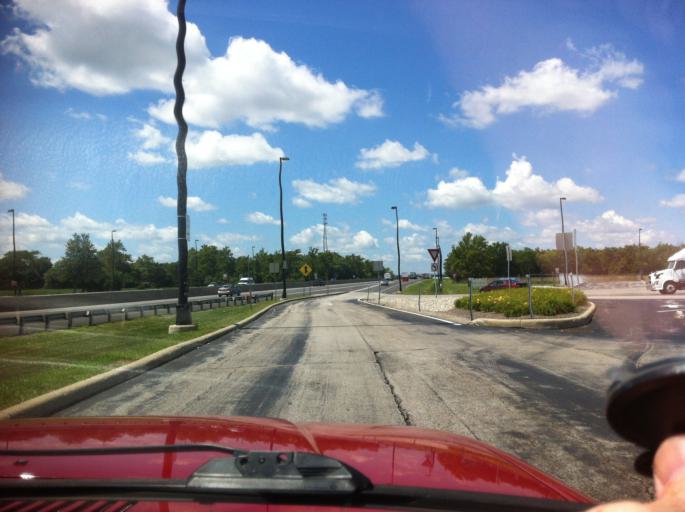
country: US
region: Ohio
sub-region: Ottawa County
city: Genoa
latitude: 41.4910
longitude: -83.3692
